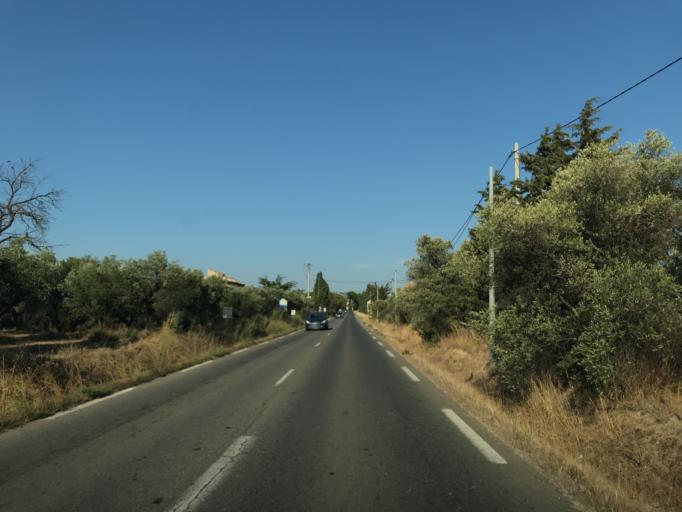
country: FR
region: Provence-Alpes-Cote d'Azur
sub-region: Departement des Bouches-du-Rhone
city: La Fare-les-Oliviers
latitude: 43.5472
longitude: 5.1661
